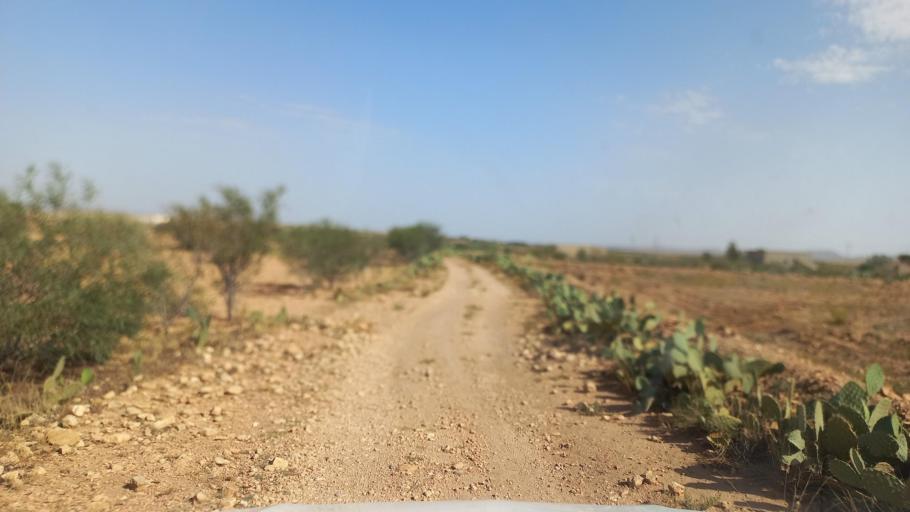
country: TN
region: Al Qasrayn
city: Kasserine
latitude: 35.2810
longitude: 8.9532
